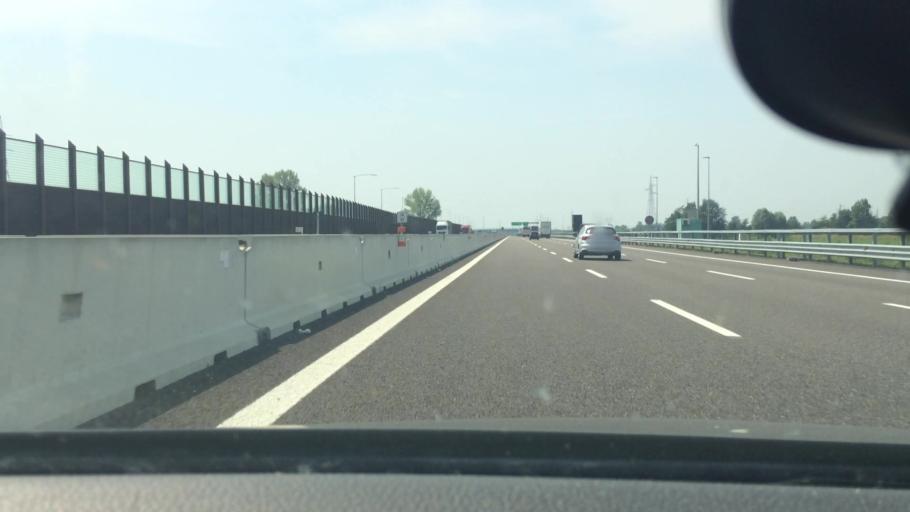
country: IT
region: Lombardy
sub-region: Provincia di Lodi
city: Merlino
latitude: 45.4390
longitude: 9.4252
